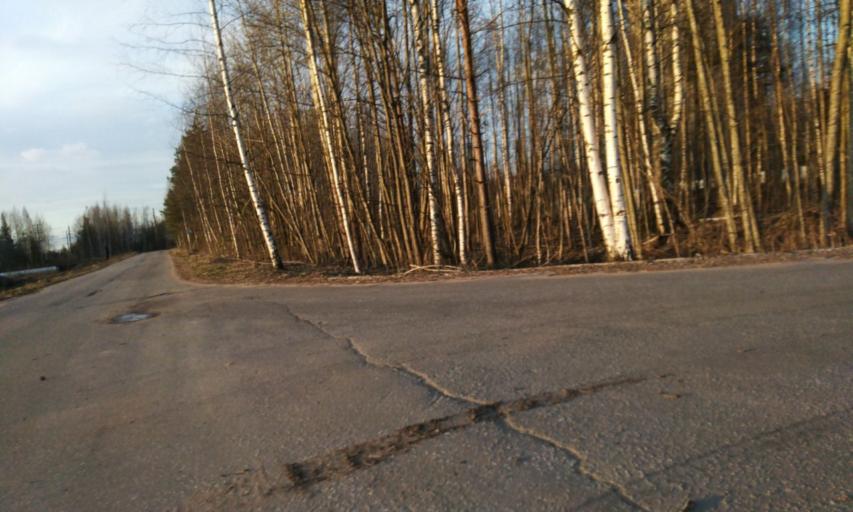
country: RU
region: Leningrad
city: Novoye Devyatkino
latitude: 60.0770
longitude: 30.4671
